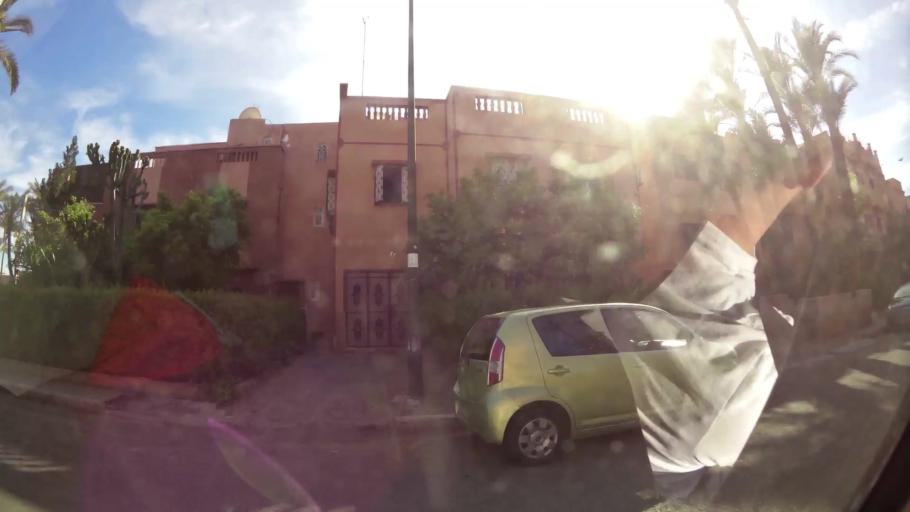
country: MA
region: Marrakech-Tensift-Al Haouz
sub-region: Marrakech
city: Marrakesh
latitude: 31.6587
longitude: -8.0120
